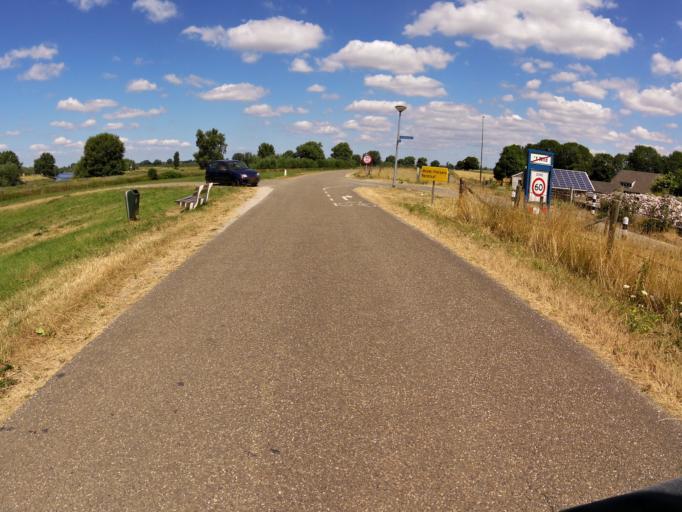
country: NL
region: Gelderland
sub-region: Gemeente Maasdriel
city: Heerewaarden
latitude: 51.7662
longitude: 5.3638
